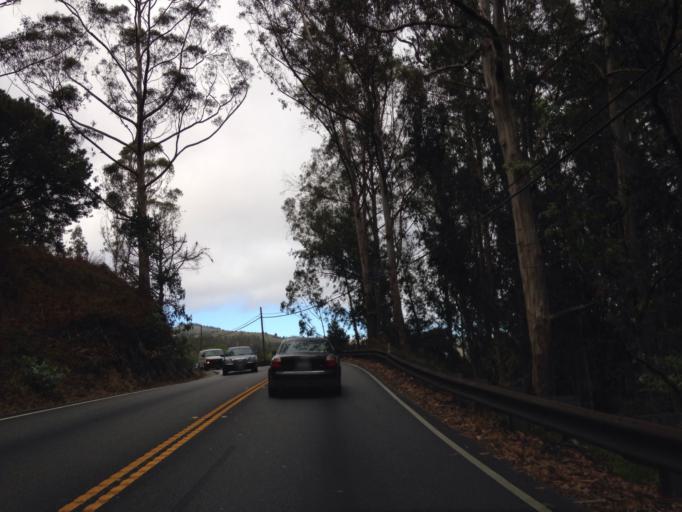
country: US
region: California
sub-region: San Mateo County
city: Half Moon Bay
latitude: 37.4725
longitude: -122.4207
